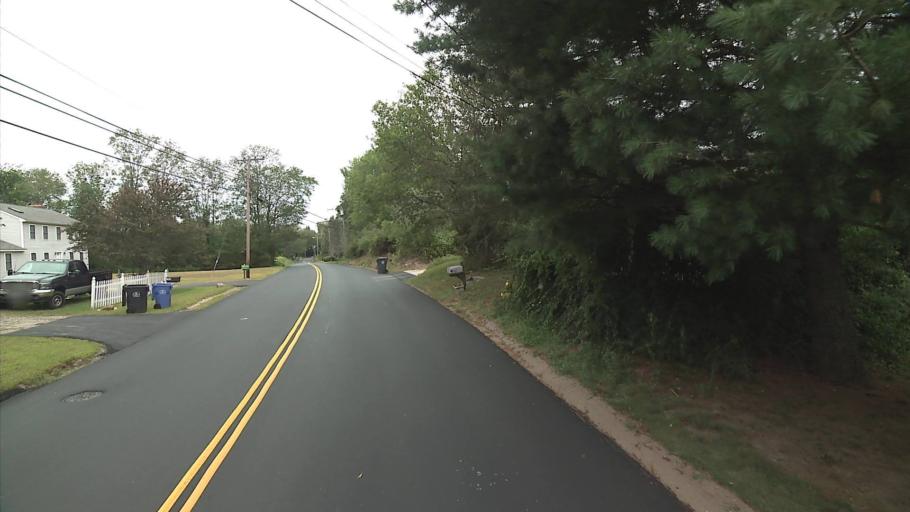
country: US
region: Connecticut
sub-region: New London County
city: Colchester
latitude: 41.5824
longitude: -72.3366
